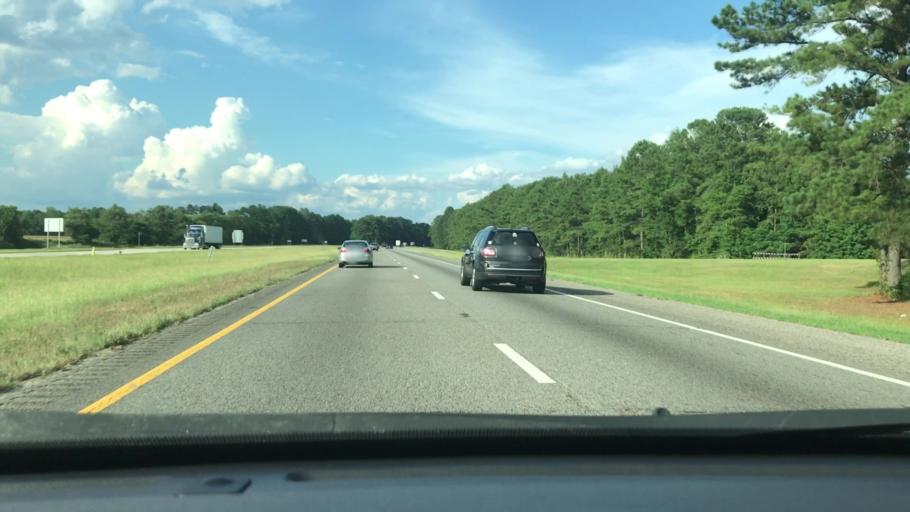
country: US
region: South Carolina
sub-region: Dillon County
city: Dillon
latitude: 34.4197
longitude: -79.4116
